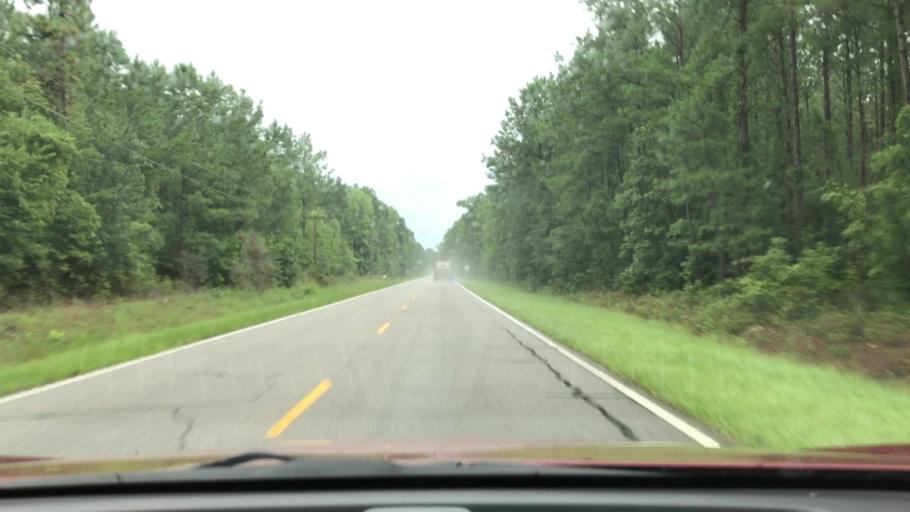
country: US
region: South Carolina
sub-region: Georgetown County
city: Georgetown
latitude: 33.4878
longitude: -79.2663
